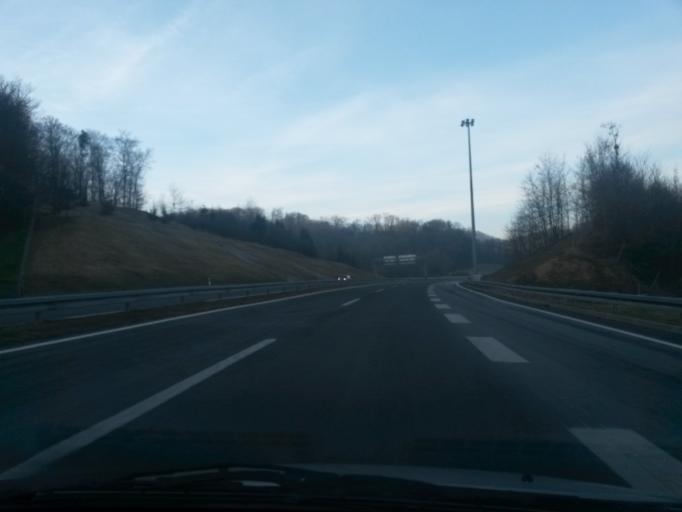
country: HR
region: Varazdinska
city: Ljubescica
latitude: 46.2105
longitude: 16.4065
